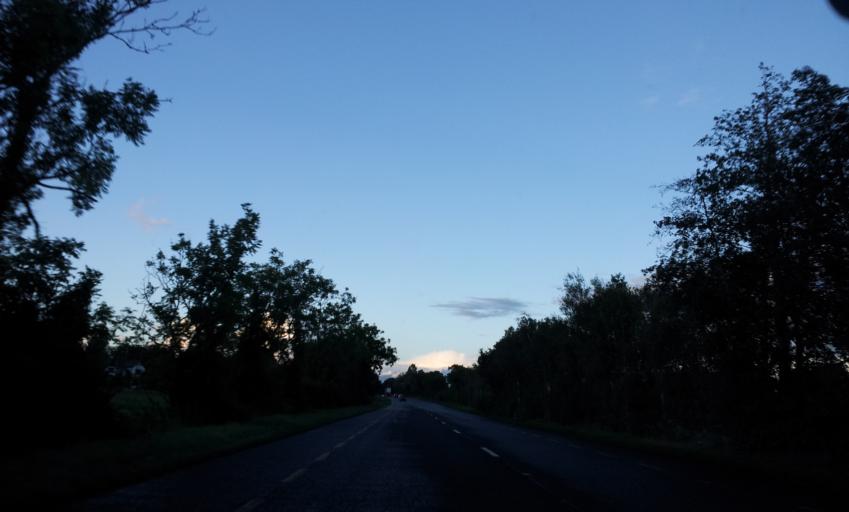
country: IE
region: Munster
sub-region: County Limerick
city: Rathkeale
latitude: 52.4961
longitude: -8.9968
